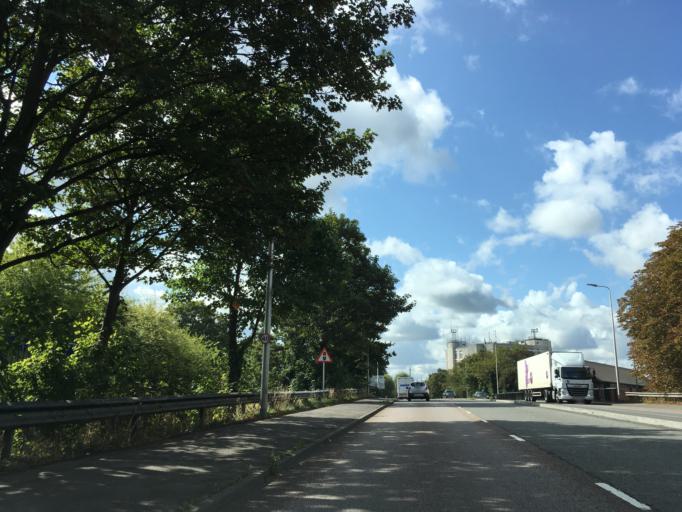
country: GB
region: England
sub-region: West Berkshire
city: Newbury
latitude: 51.4027
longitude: -1.3193
